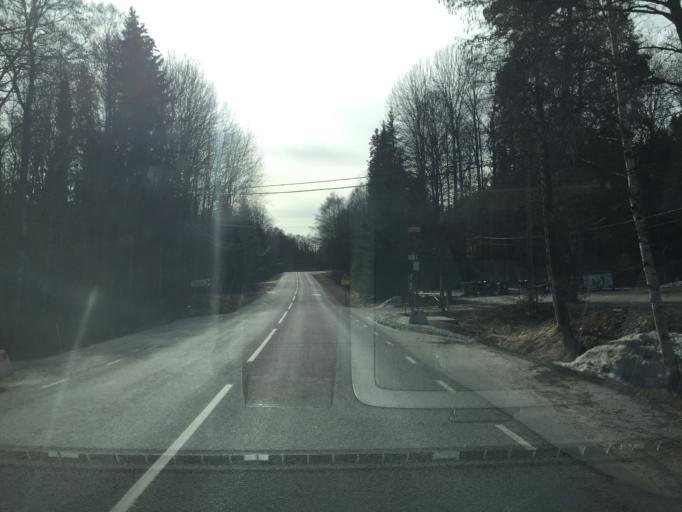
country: SE
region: Stockholm
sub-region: Haninge Kommun
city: Jordbro
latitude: 59.1181
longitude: 18.0174
